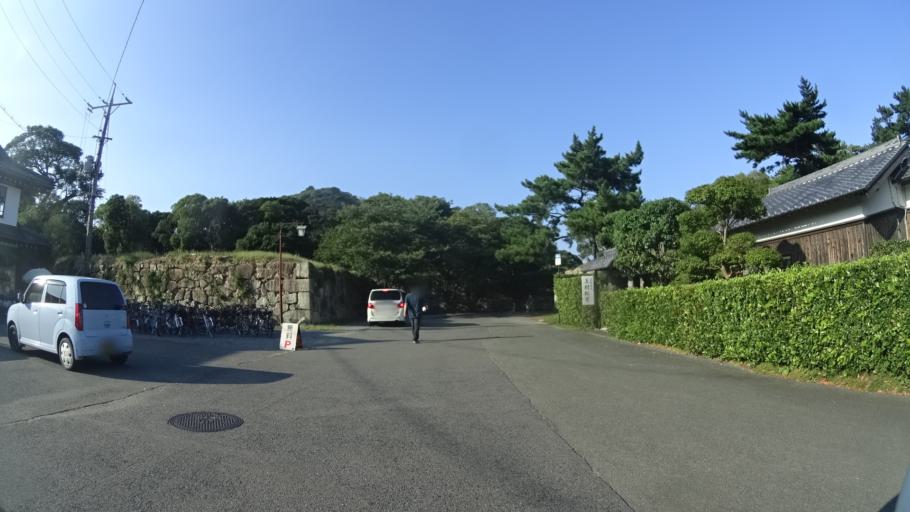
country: JP
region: Yamaguchi
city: Hagi
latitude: 34.4157
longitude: 131.3827
